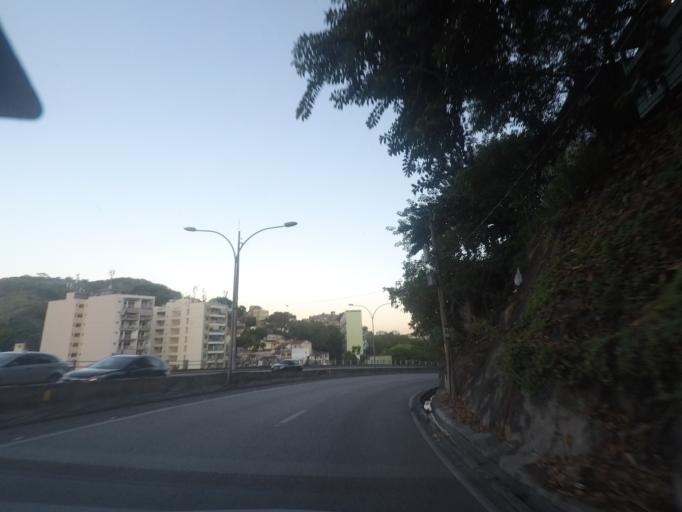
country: BR
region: Rio de Janeiro
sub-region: Rio De Janeiro
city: Rio de Janeiro
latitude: -22.9149
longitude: -43.2644
